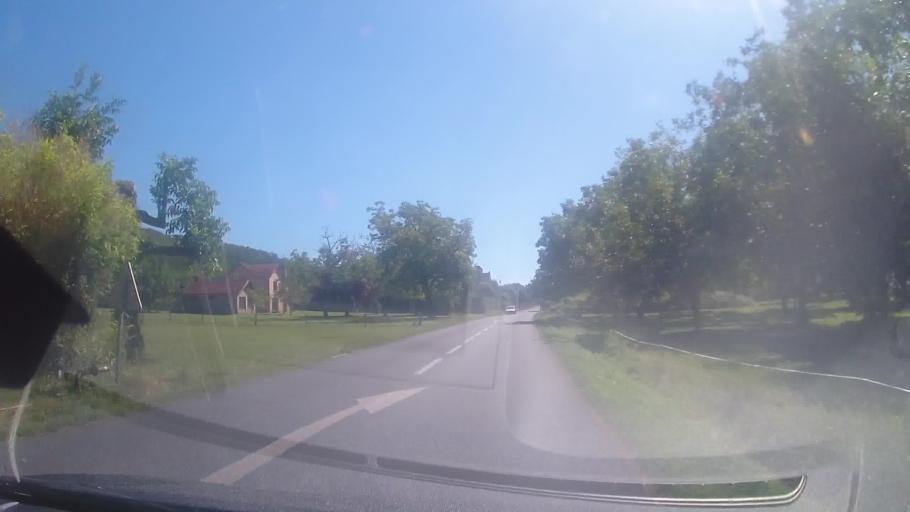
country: FR
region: Aquitaine
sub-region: Departement de la Dordogne
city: Cenac-et-Saint-Julien
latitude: 44.8232
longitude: 1.1872
